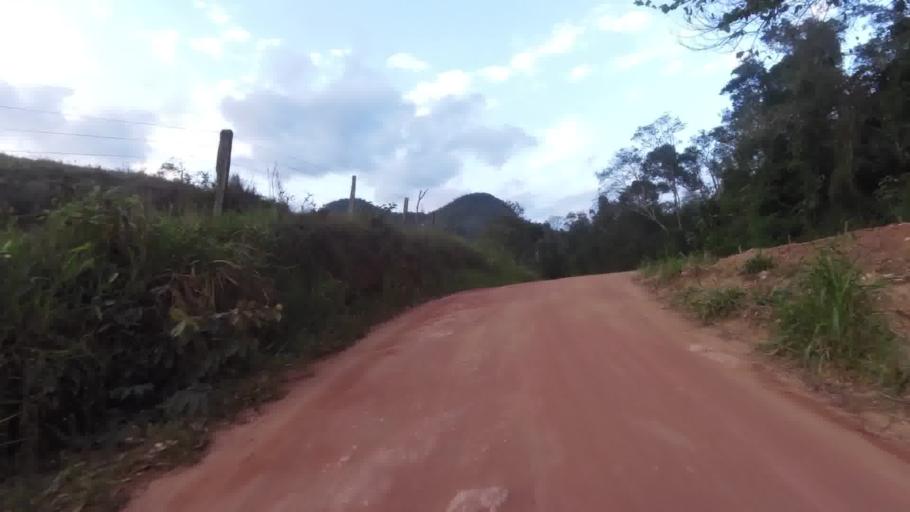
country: BR
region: Espirito Santo
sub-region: Guarapari
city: Guarapari
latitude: -20.6683
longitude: -40.6101
